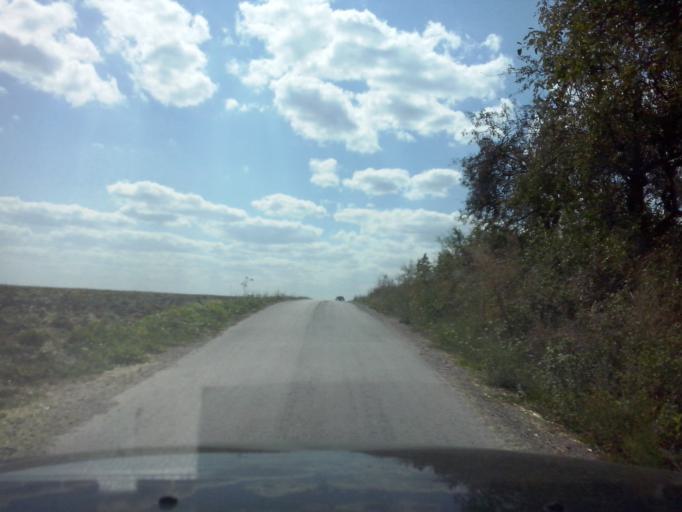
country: PL
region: Swietokrzyskie
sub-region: Powiat staszowski
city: Szydlow
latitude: 50.6051
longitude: 21.0693
